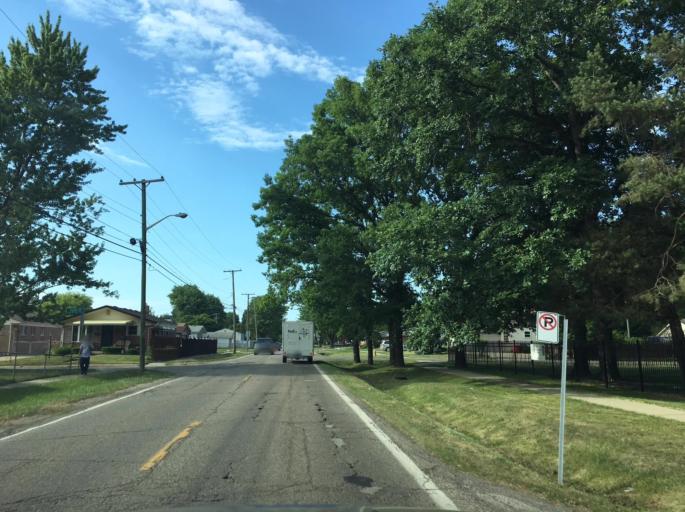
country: US
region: Michigan
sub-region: Macomb County
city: Fraser
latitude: 42.5454
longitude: -82.9199
